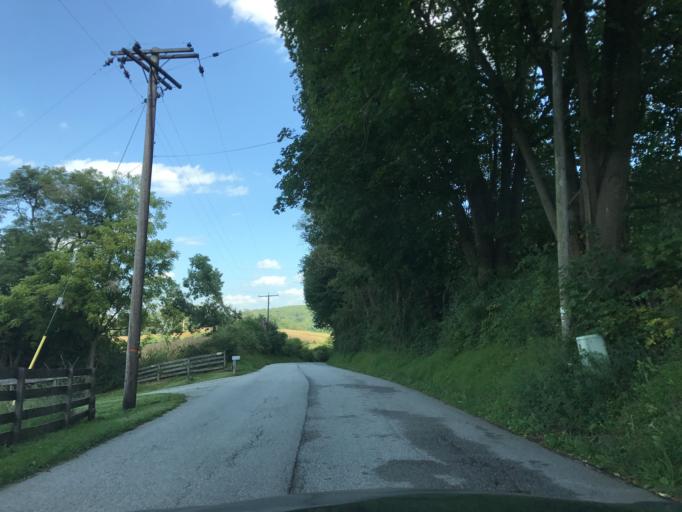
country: US
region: Pennsylvania
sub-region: York County
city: New Freedom
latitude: 39.6529
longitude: -76.6334
